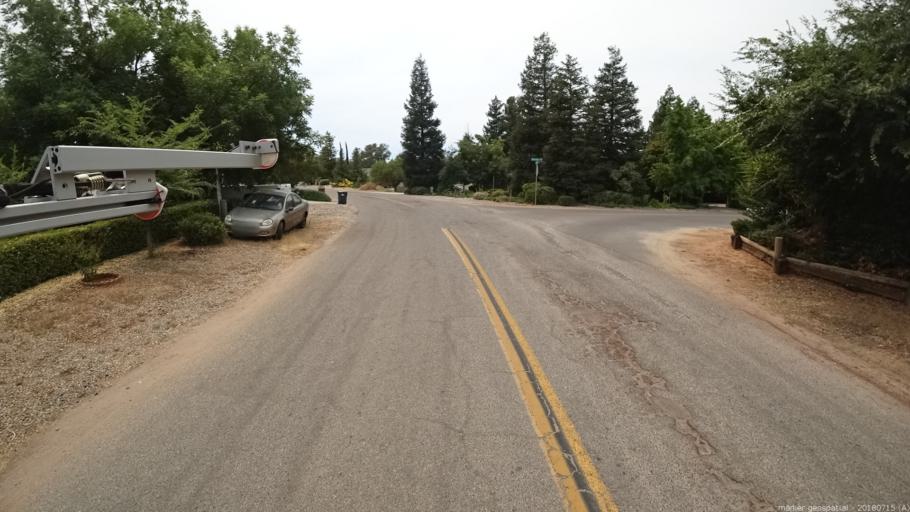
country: US
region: California
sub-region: Madera County
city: Madera Acres
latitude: 37.0223
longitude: -120.0773
